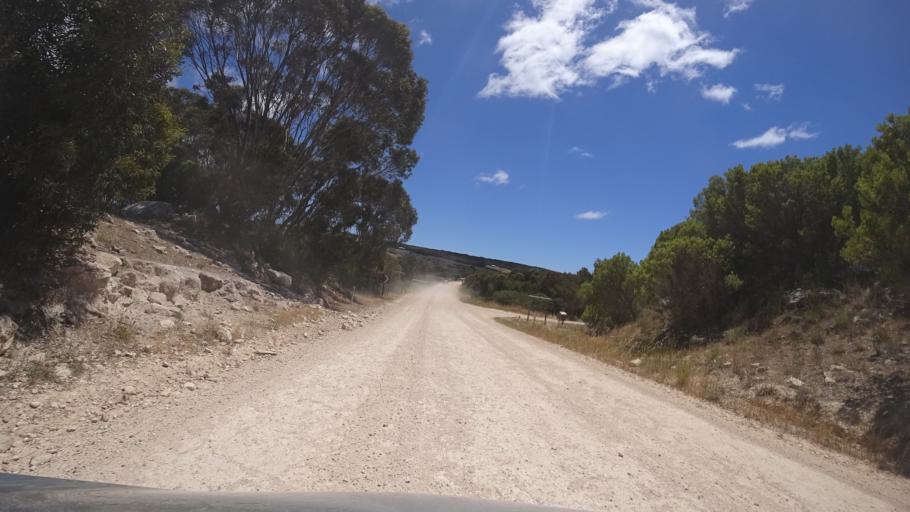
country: AU
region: South Australia
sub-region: Yankalilla
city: Normanville
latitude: -35.8015
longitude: 138.0663
